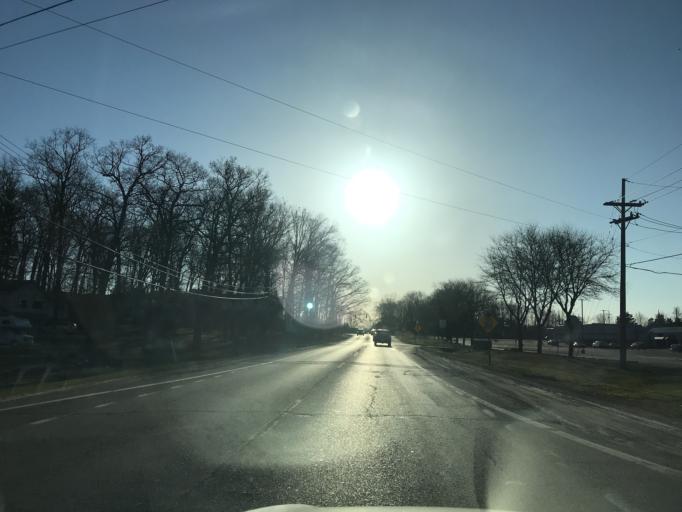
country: US
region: Michigan
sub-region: Oakland County
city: Walled Lake
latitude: 42.5255
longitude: -83.4971
